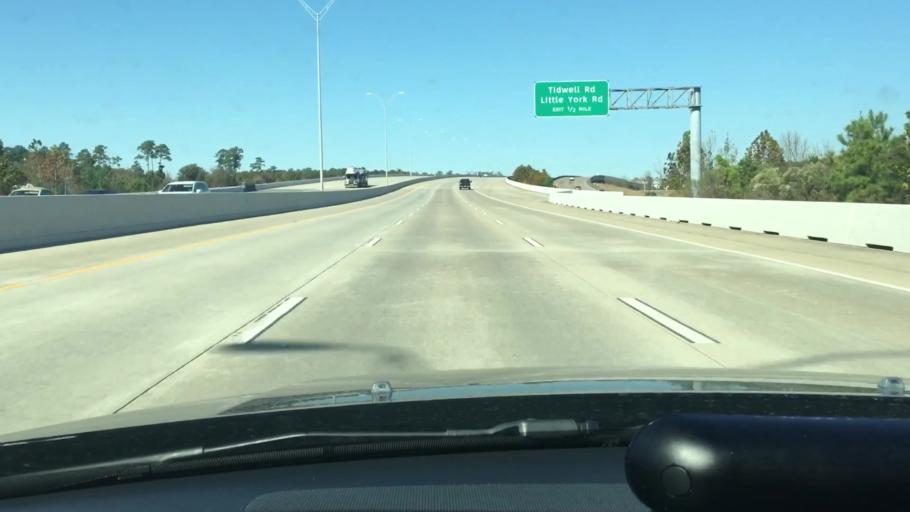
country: US
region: Texas
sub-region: Harris County
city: Sheldon
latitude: 29.8397
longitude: -95.1824
